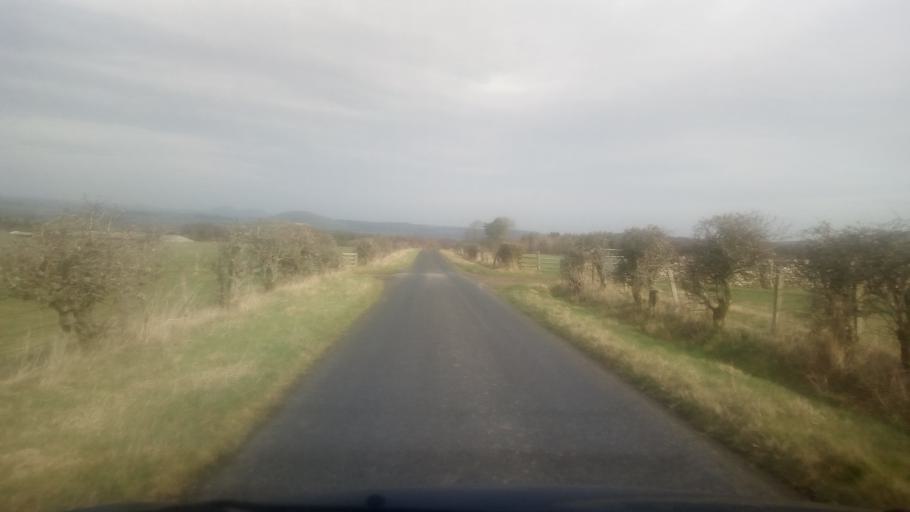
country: GB
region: Scotland
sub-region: The Scottish Borders
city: Hawick
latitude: 55.4209
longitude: -2.7031
